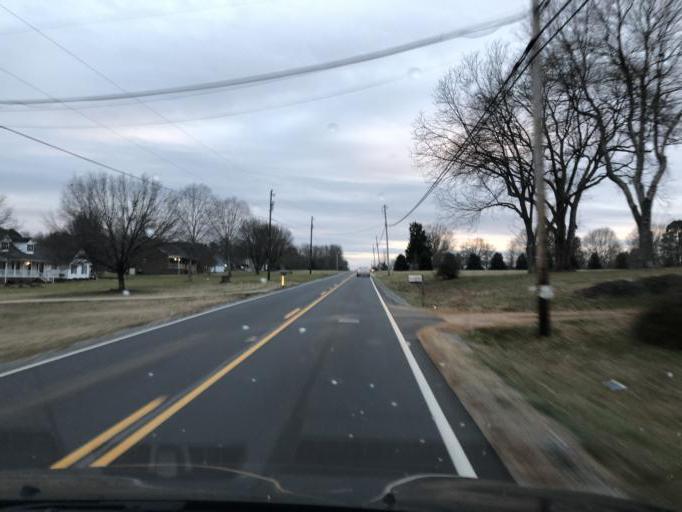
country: US
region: North Carolina
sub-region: Cleveland County
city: Shelby
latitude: 35.2579
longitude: -81.5227
